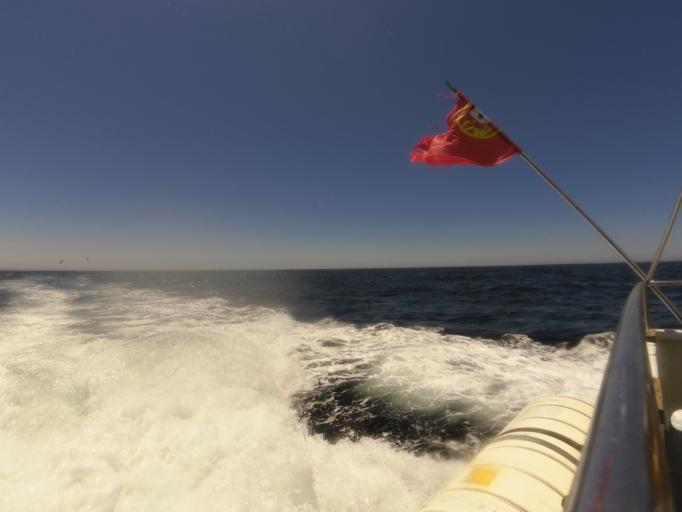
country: PT
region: Leiria
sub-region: Peniche
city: Peniche
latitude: 39.4077
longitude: -9.4981
